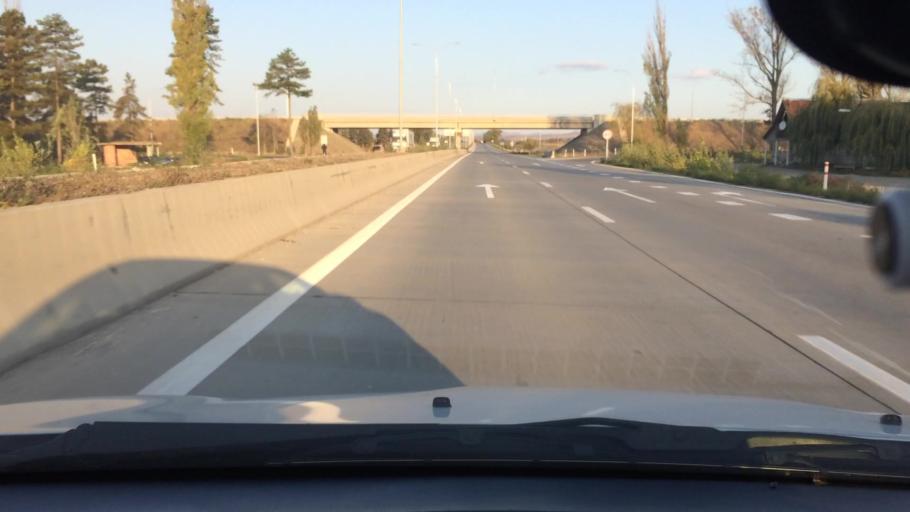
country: GE
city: Agara
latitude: 42.0507
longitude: 43.9092
